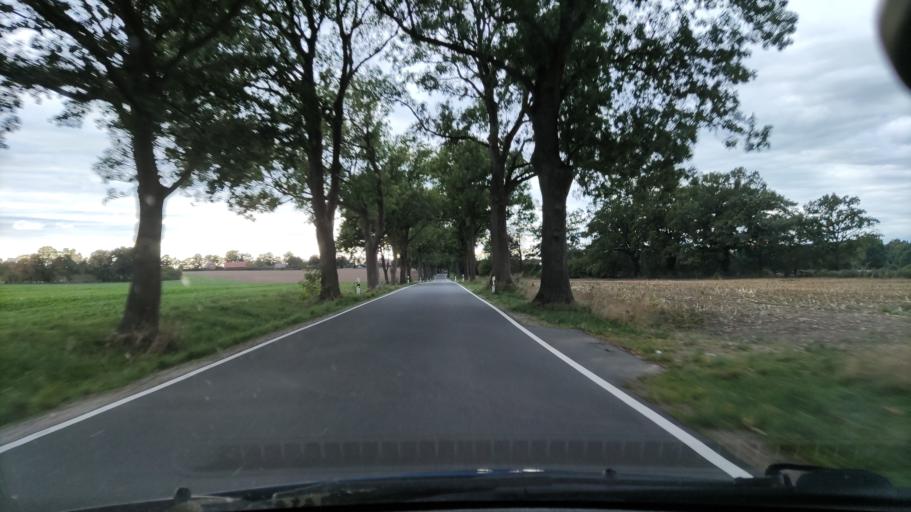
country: DE
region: Mecklenburg-Vorpommern
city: Wittenburg
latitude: 53.4617
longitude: 10.9860
